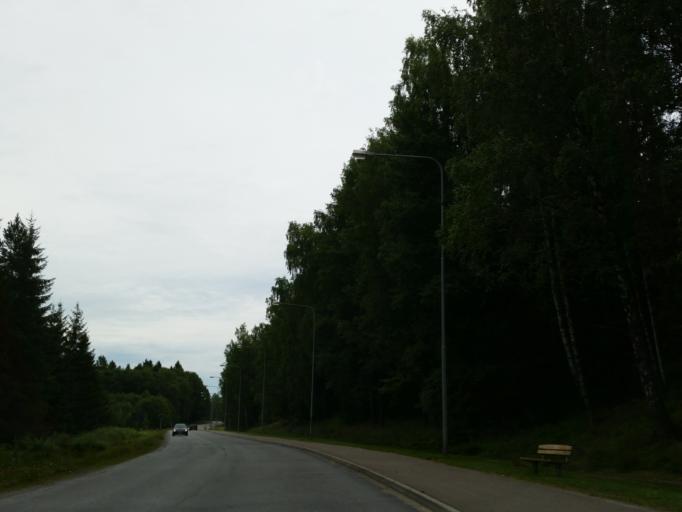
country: SE
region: Stockholm
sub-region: Nykvarns Kommun
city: Nykvarn
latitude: 59.1746
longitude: 17.4445
